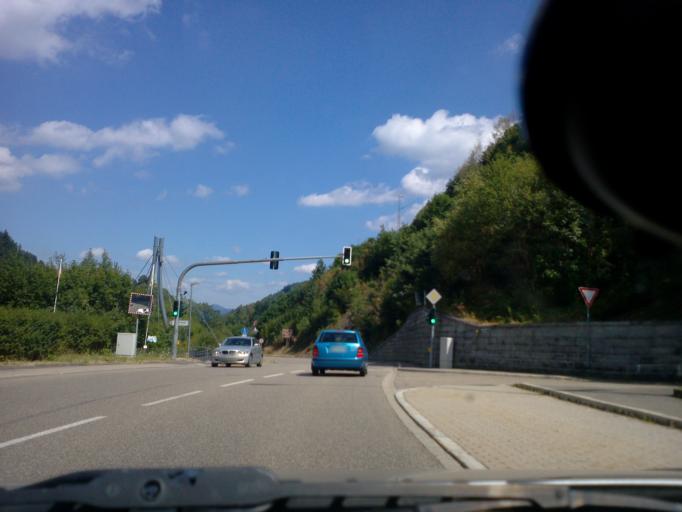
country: DE
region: Baden-Wuerttemberg
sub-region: Freiburg Region
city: Hornberg
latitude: 48.2014
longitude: 8.2352
